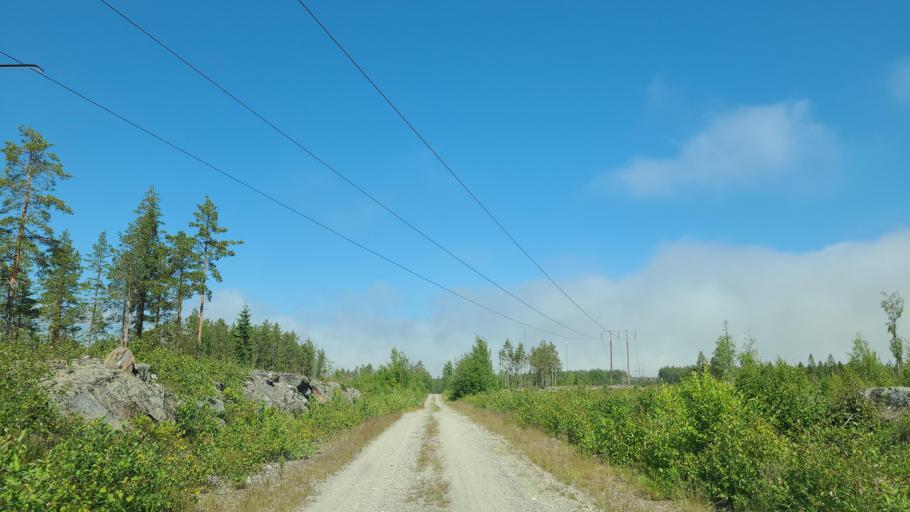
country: SE
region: Vaesternorrland
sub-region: OErnskoeldsviks Kommun
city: Husum
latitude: 63.4409
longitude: 19.2339
